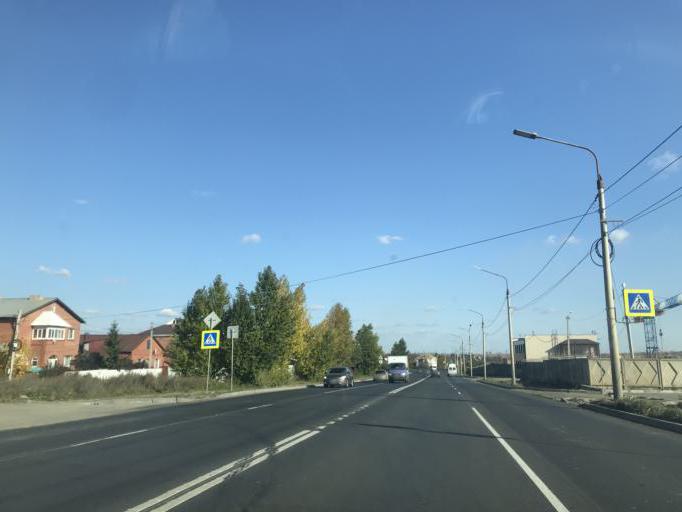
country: RU
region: Chelyabinsk
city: Roshchino
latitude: 55.2346
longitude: 61.3115
